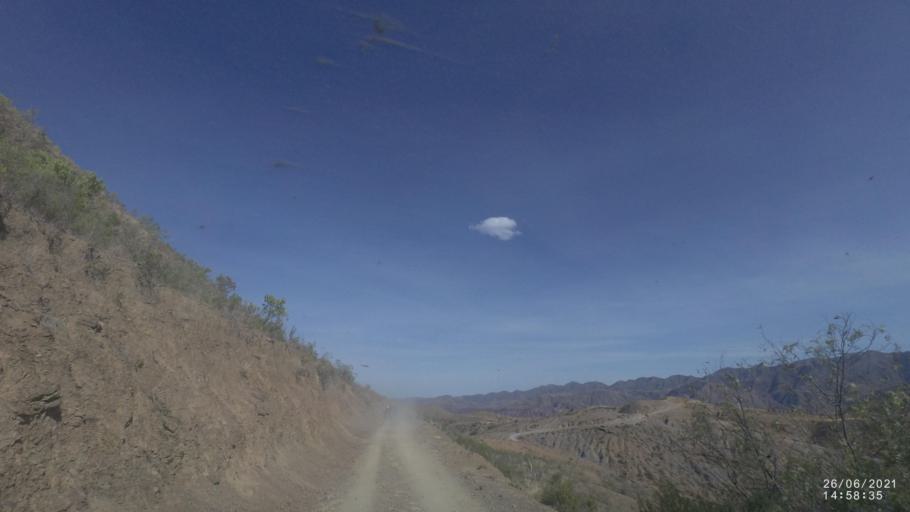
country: BO
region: Cochabamba
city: Mizque
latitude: -17.9449
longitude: -65.6194
